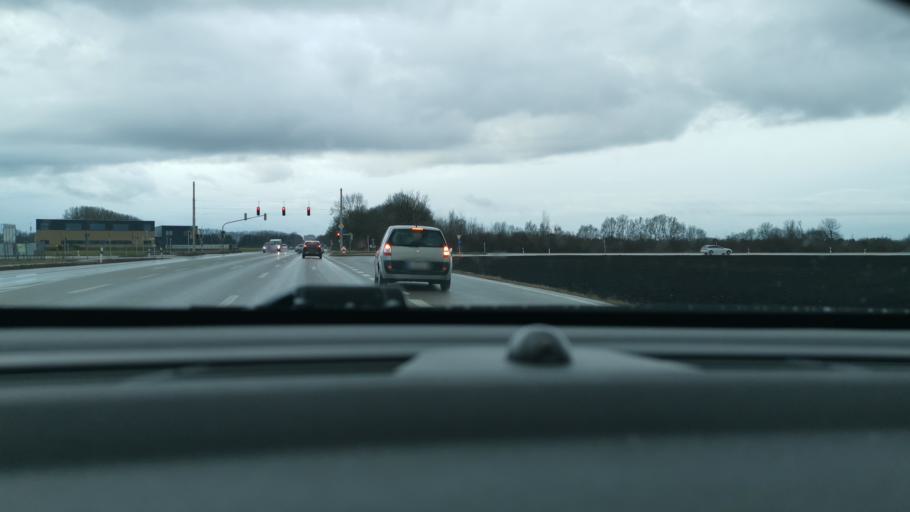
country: DE
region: Bavaria
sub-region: Swabia
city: Gersthofen
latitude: 48.4220
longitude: 10.9199
